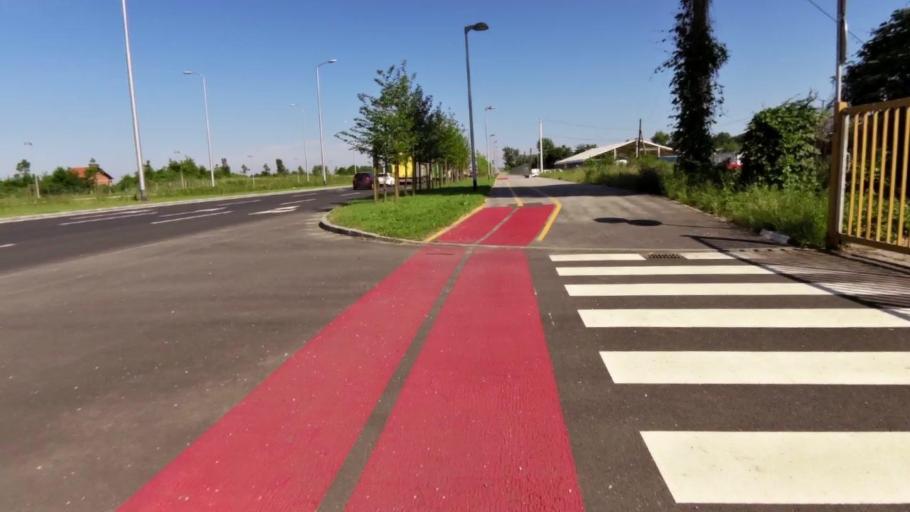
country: HR
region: Zagrebacka
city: Micevec
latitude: 45.7841
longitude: 16.0431
